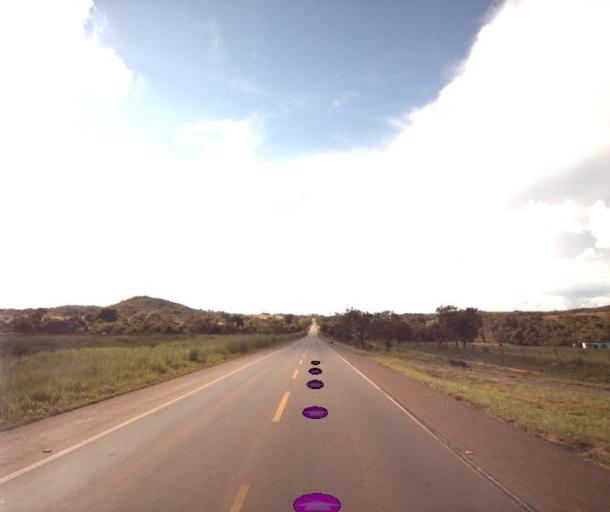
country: BR
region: Goias
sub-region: Rialma
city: Rialma
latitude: -15.4406
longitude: -49.5085
